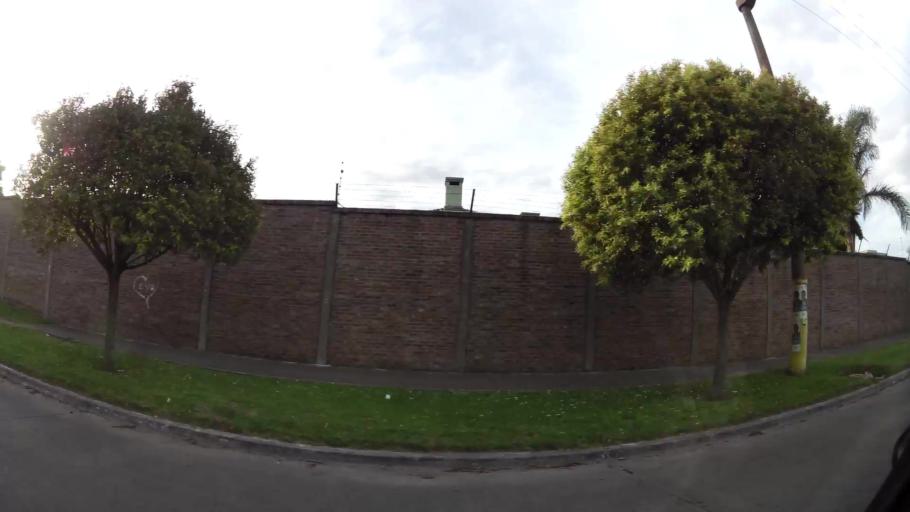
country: AR
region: Buenos Aires
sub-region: Partido de Quilmes
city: Quilmes
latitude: -34.7226
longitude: -58.2400
